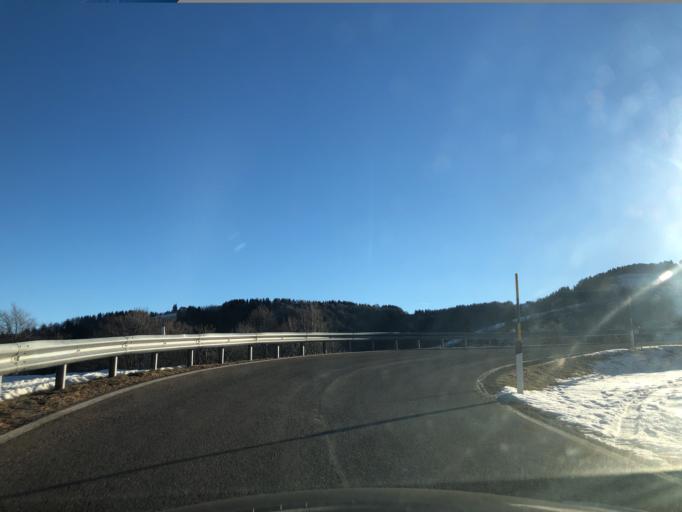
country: IT
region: Trentino-Alto Adige
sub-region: Provincia di Trento
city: Brentonico
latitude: 45.7852
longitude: 10.9142
